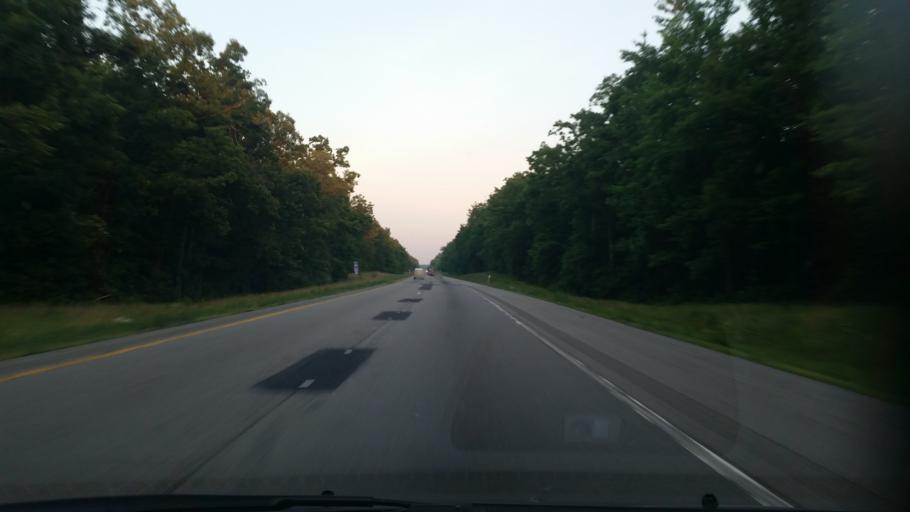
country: US
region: Tennessee
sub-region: Putnam County
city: Monterey
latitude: 36.0873
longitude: -85.2229
